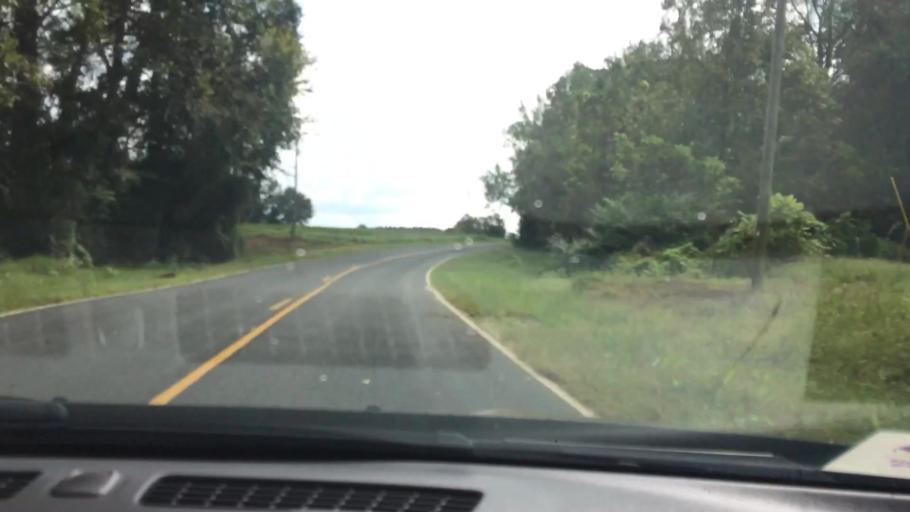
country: US
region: North Carolina
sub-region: Greene County
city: Maury
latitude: 35.4947
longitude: -77.5211
